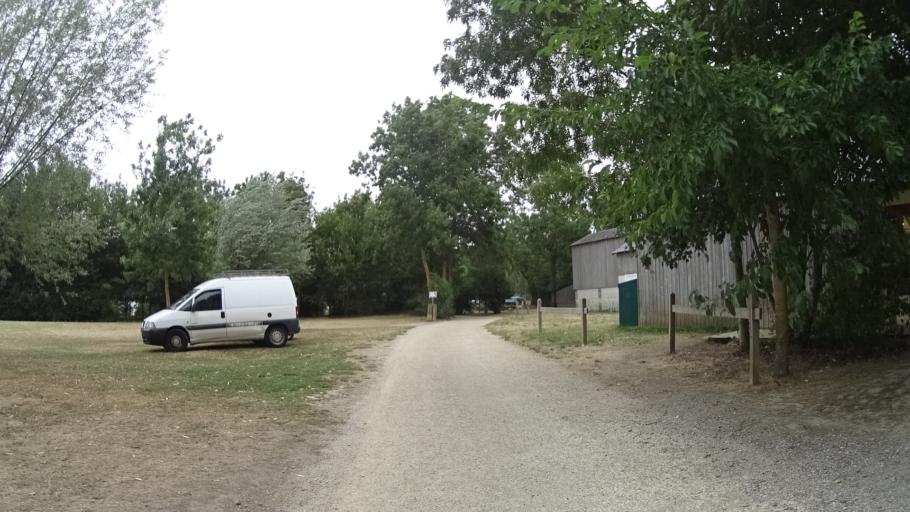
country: FR
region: Pays de la Loire
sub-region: Departement de Maine-et-Loire
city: La Possonniere
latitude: 47.3709
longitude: -0.6848
